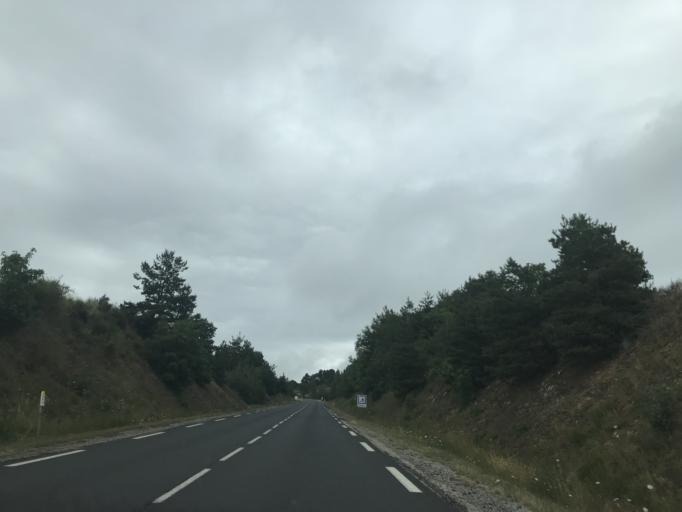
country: FR
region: Auvergne
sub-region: Departement de la Haute-Loire
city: Saint-Paulien
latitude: 45.1631
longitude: 3.8344
